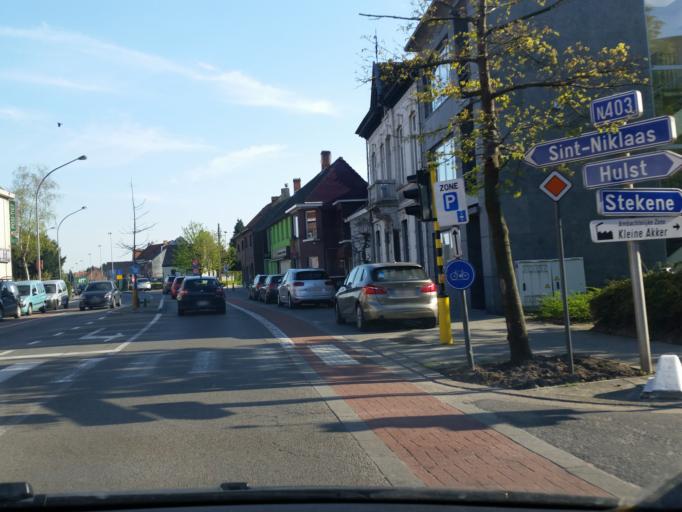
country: BE
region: Flanders
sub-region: Provincie Oost-Vlaanderen
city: Stekene
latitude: 51.2061
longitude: 4.0757
